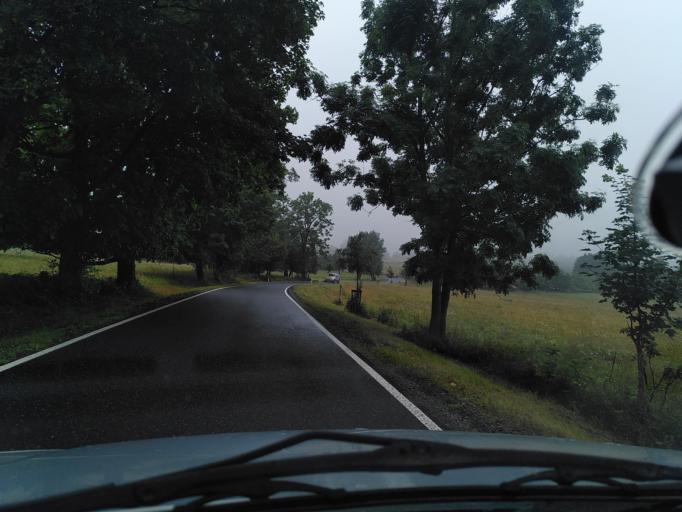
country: CZ
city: Kamenicky Senov
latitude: 50.7738
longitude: 14.4896
